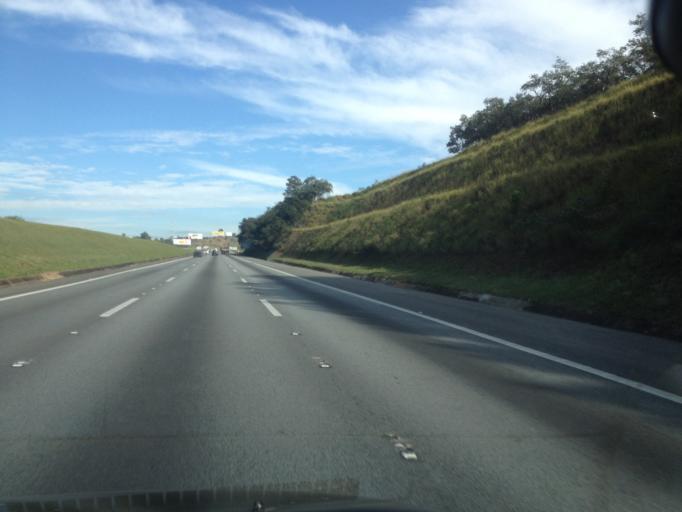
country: BR
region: Sao Paulo
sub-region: Mairinque
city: Mairinque
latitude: -23.4212
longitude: -47.2304
